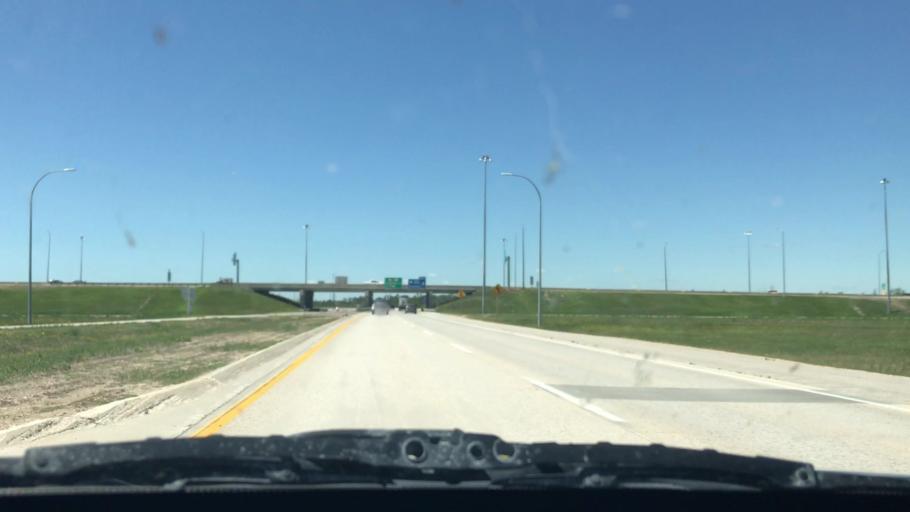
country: CA
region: Manitoba
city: Winnipeg
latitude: 49.8334
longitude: -96.9604
